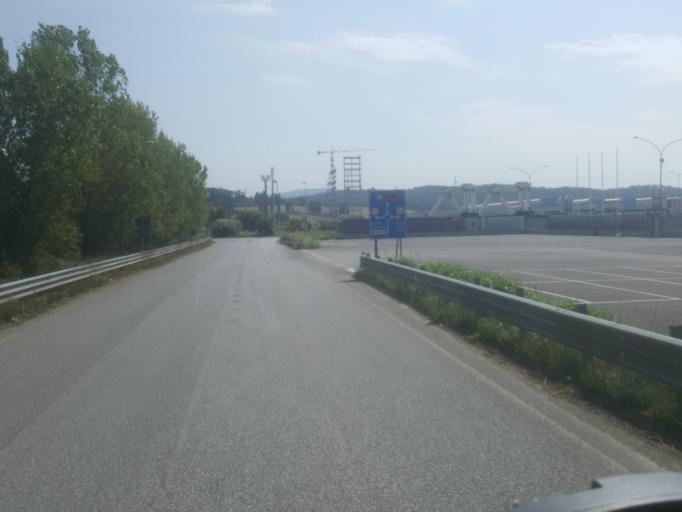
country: IT
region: Tuscany
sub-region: Provincia di Livorno
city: Guasticce
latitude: 43.5988
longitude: 10.4008
